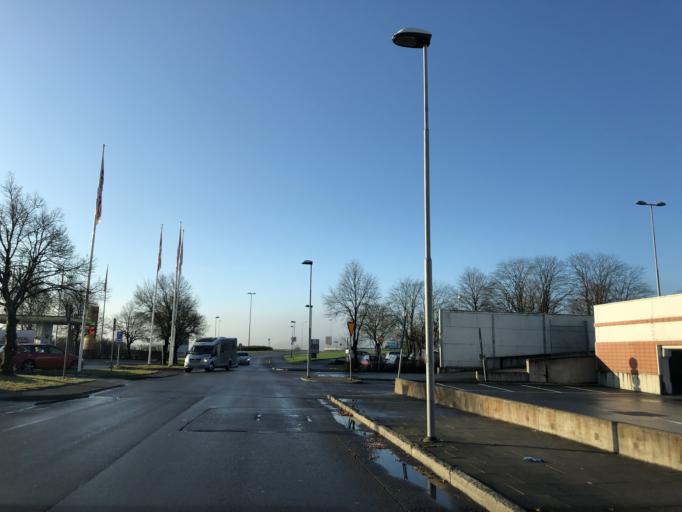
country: SE
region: Vaestra Goetaland
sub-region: Goteborg
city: Hammarkullen
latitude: 57.7944
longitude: 12.0499
